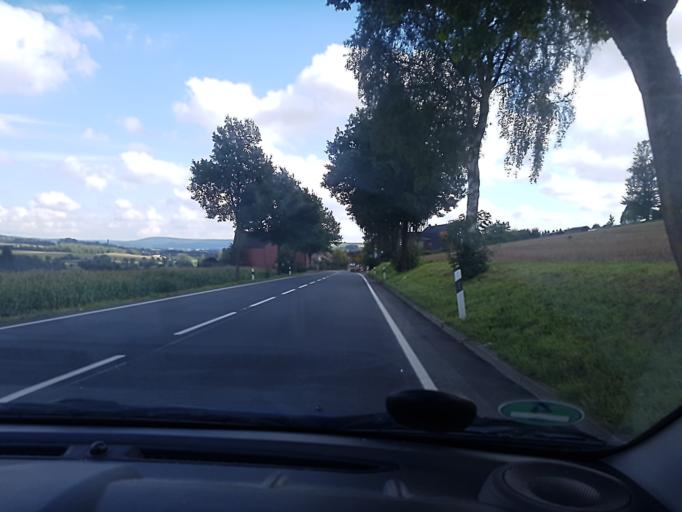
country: DE
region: Lower Saxony
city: Bodenfelde
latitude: 51.6805
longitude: 9.5727
